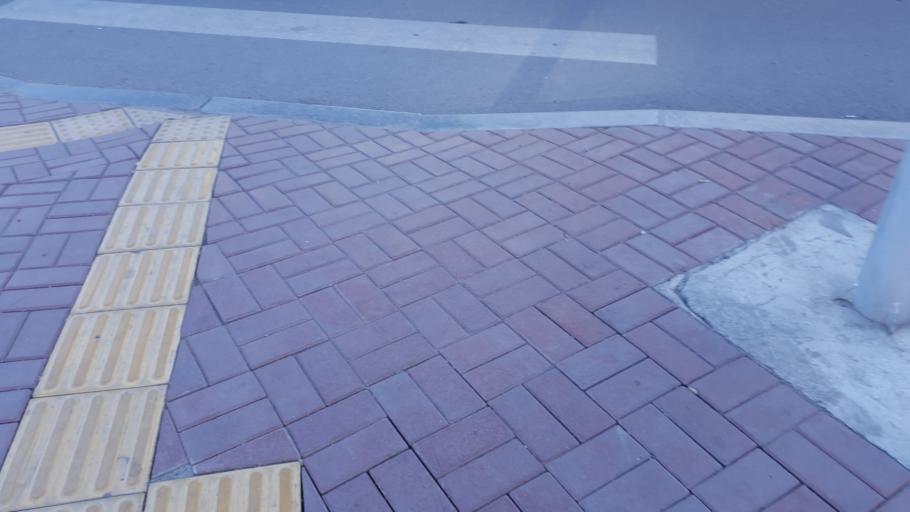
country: MN
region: Ulaanbaatar
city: Ulaanbaatar
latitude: 47.8962
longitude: 106.9085
